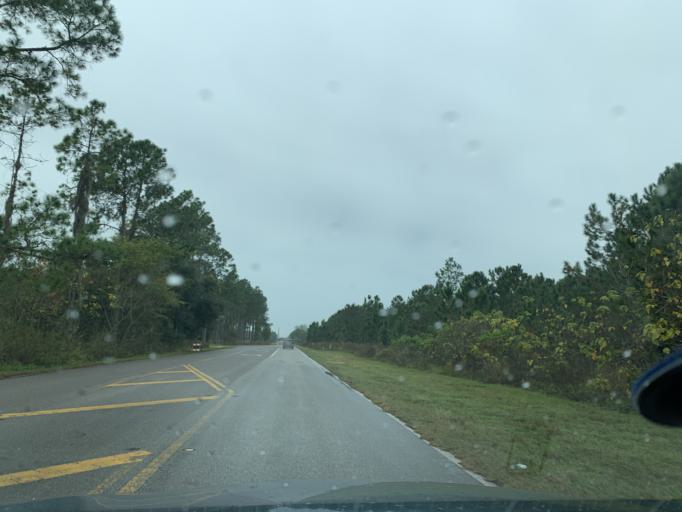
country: US
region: Florida
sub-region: Pasco County
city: Wesley Chapel
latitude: 28.2735
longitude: -82.3218
